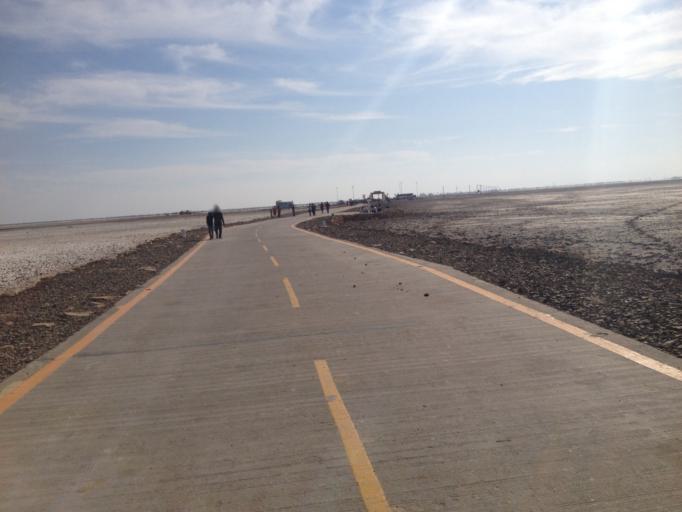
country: IN
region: Gujarat
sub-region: Kachchh
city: Bhuj
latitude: 23.8314
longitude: 69.5215
